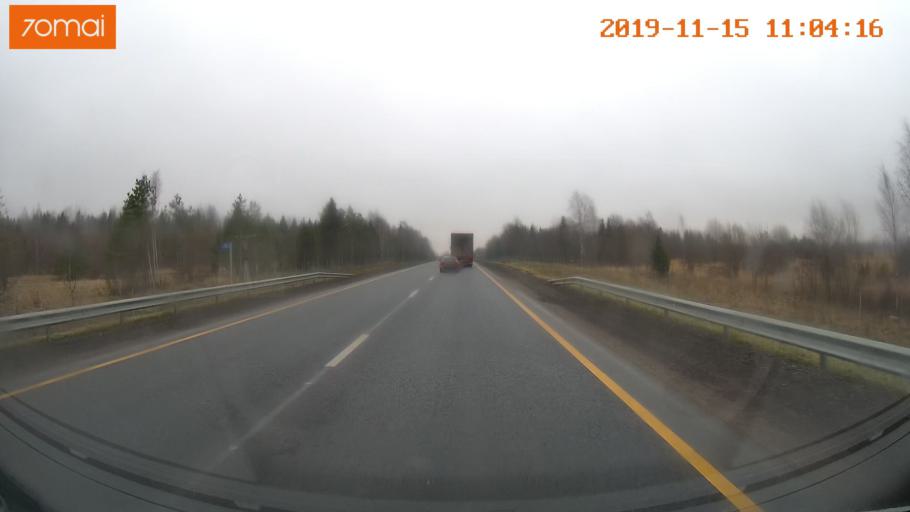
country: RU
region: Vologda
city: Chebsara
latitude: 59.1209
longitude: 38.9800
